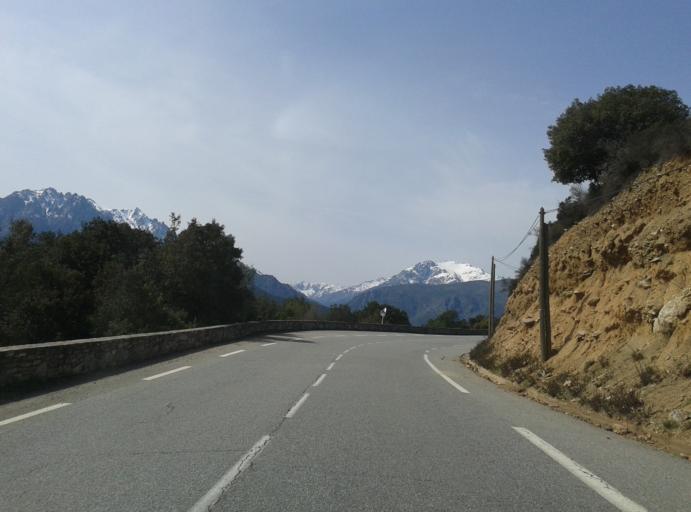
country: FR
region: Corsica
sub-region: Departement de la Haute-Corse
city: Morosaglia
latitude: 42.4841
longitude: 9.1949
